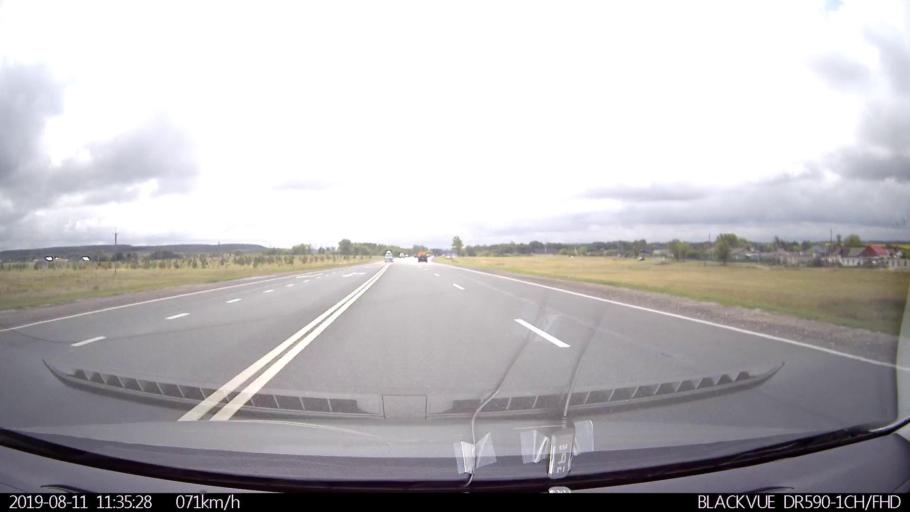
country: RU
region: Ulyanovsk
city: Silikatnyy
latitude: 54.0055
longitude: 48.2200
